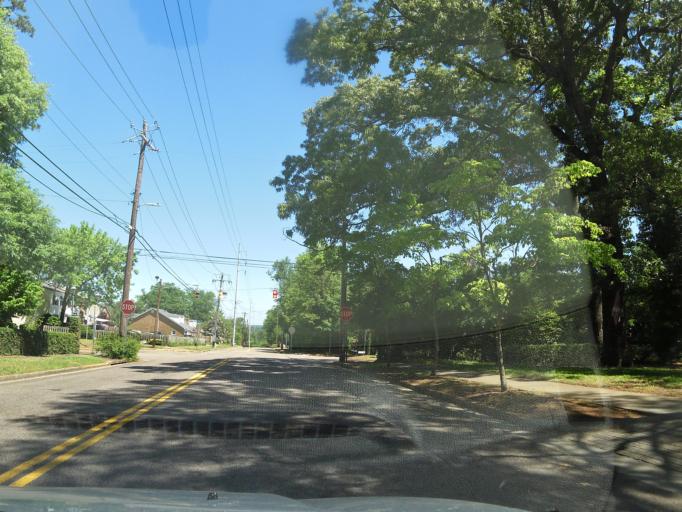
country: US
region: Georgia
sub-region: Richmond County
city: Augusta
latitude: 33.4800
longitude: -82.0269
